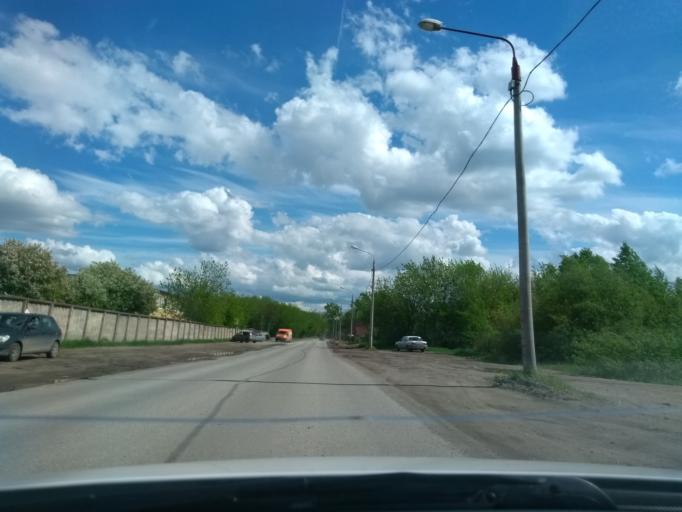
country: RU
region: Perm
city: Kondratovo
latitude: 58.0076
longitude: 56.1140
